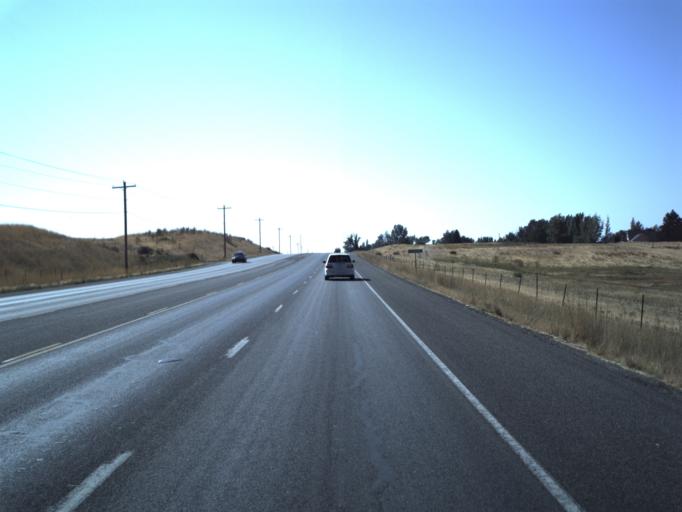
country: US
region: Utah
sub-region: Cache County
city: Hyrum
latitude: 41.6467
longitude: -111.8329
